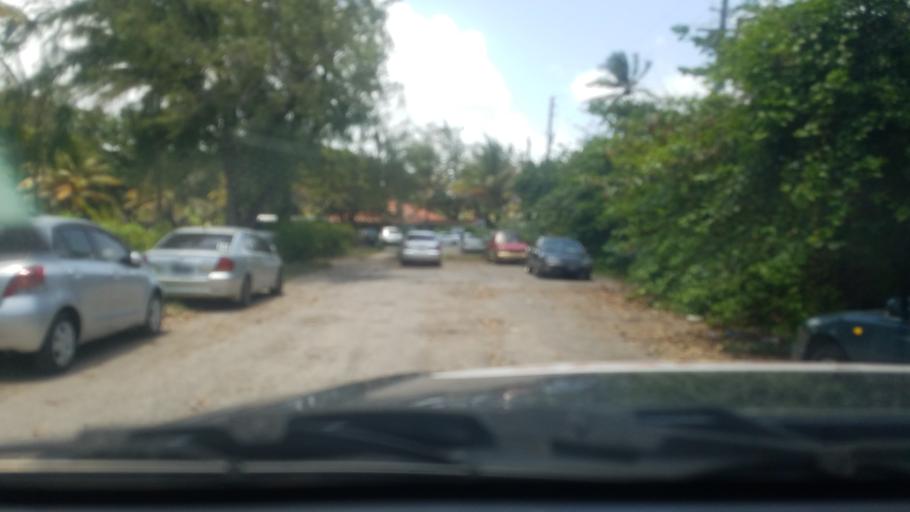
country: LC
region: Vieux-Fort
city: Vieux Fort
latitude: 13.7364
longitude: -60.9405
